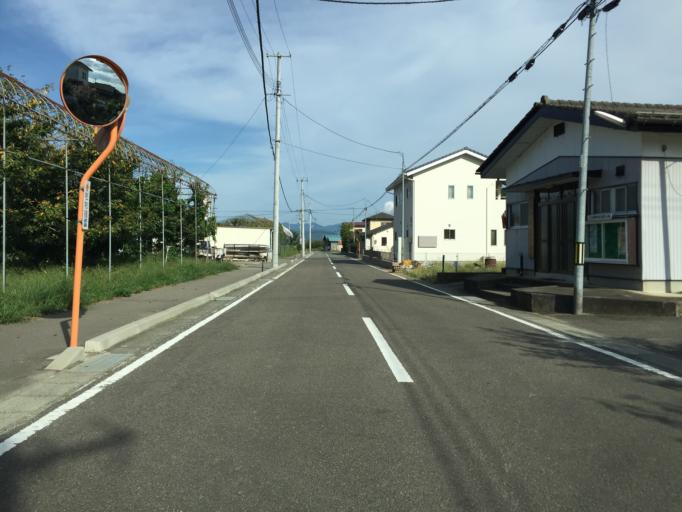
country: JP
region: Fukushima
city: Hobaramachi
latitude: 37.8166
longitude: 140.5136
